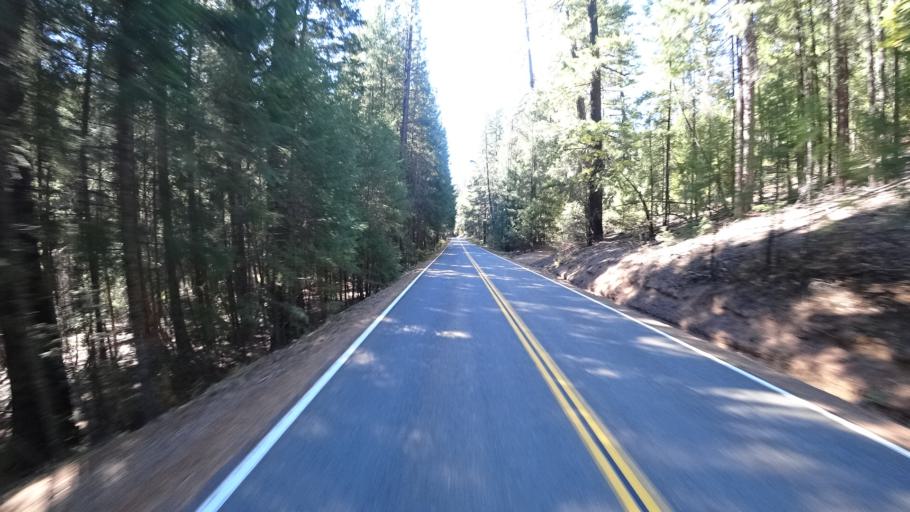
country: US
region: California
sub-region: Trinity County
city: Weaverville
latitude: 41.1996
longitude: -123.0708
